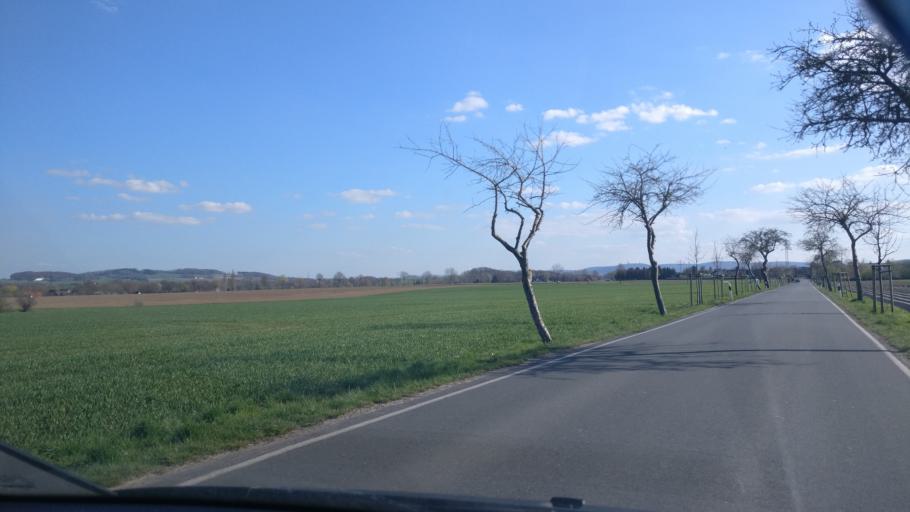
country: DE
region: North Rhine-Westphalia
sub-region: Regierungsbezirk Detmold
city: Lage
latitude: 52.0127
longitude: 8.8127
